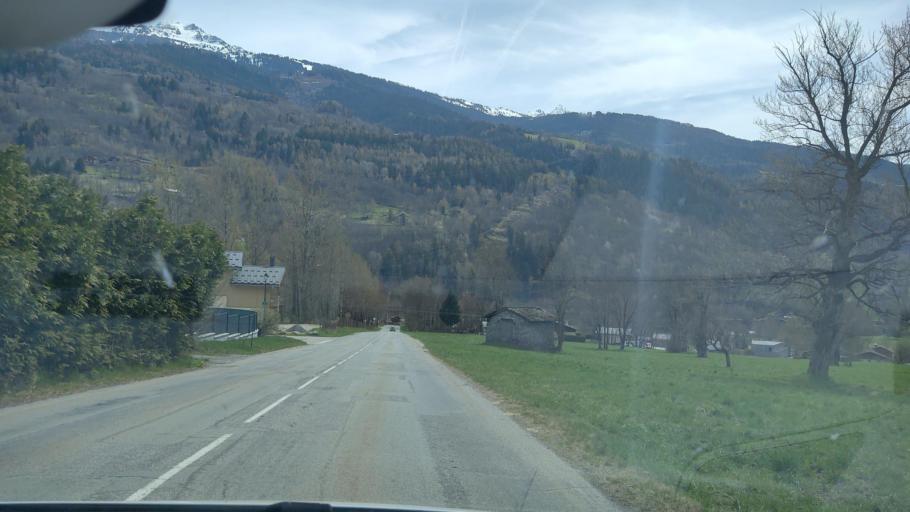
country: FR
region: Rhone-Alpes
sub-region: Departement de la Savoie
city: Bourg-Saint-Maurice
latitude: 45.6063
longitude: 6.7623
